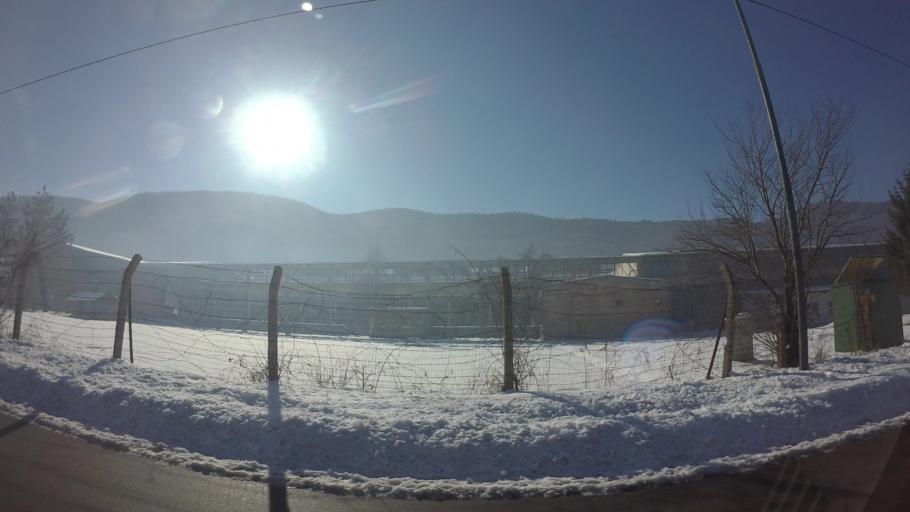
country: BA
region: Federation of Bosnia and Herzegovina
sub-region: Kanton Sarajevo
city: Sarajevo
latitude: 43.7922
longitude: 18.3324
